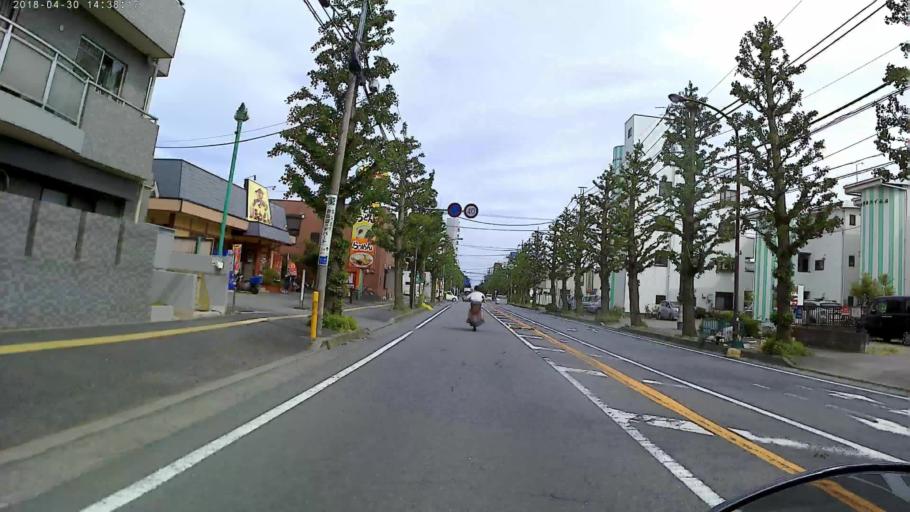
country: JP
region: Kanagawa
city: Zama
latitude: 35.5702
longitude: 139.3694
